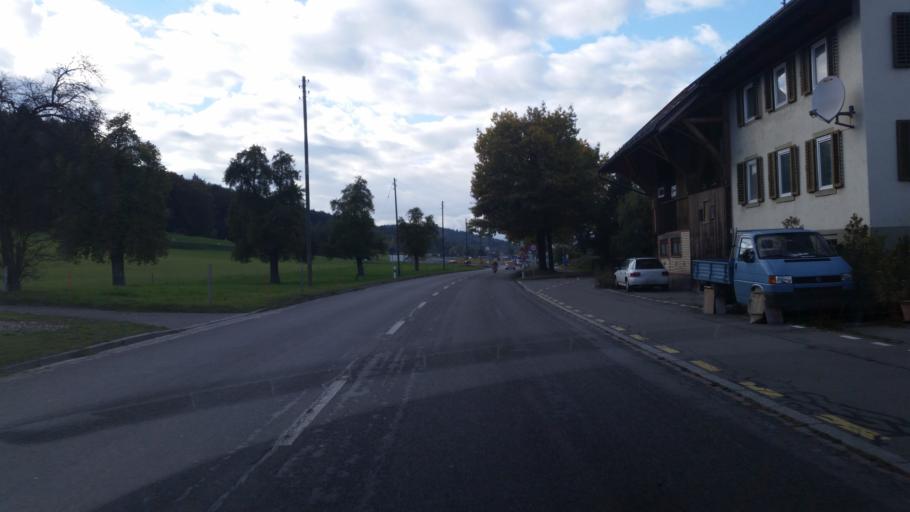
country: CH
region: Zurich
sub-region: Bezirk Zuerich
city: Zuerich (Kreis 10) / Ruetihof
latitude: 47.4236
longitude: 8.4895
